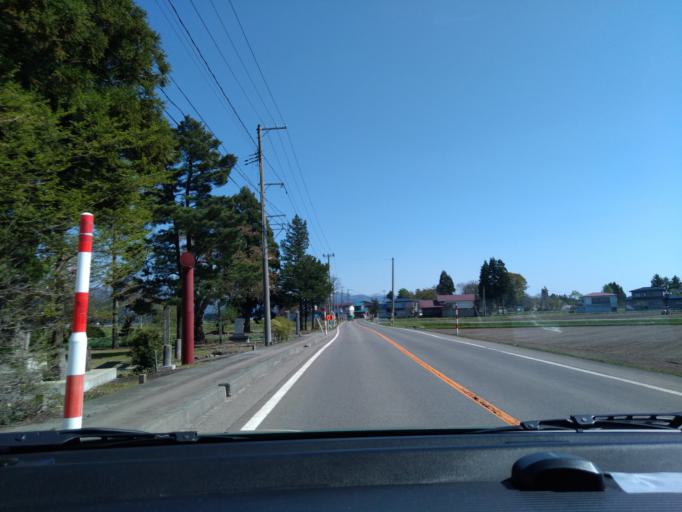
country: JP
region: Akita
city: Kakunodatemachi
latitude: 39.5693
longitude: 140.5817
